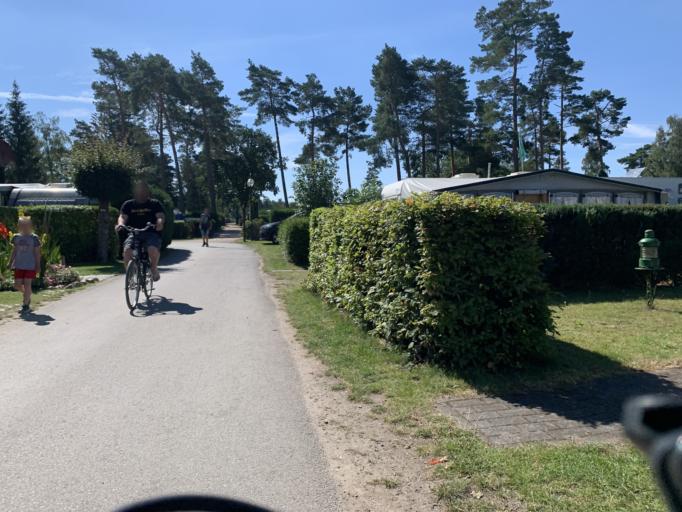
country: DE
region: Lower Saxony
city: Wietzendorf
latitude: 52.9361
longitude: 9.9631
